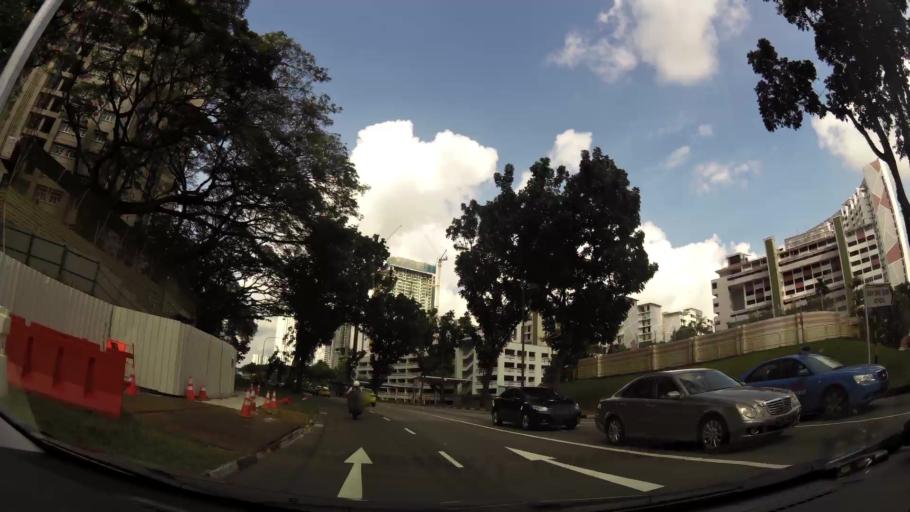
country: SG
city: Singapore
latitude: 1.2883
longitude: 103.8225
